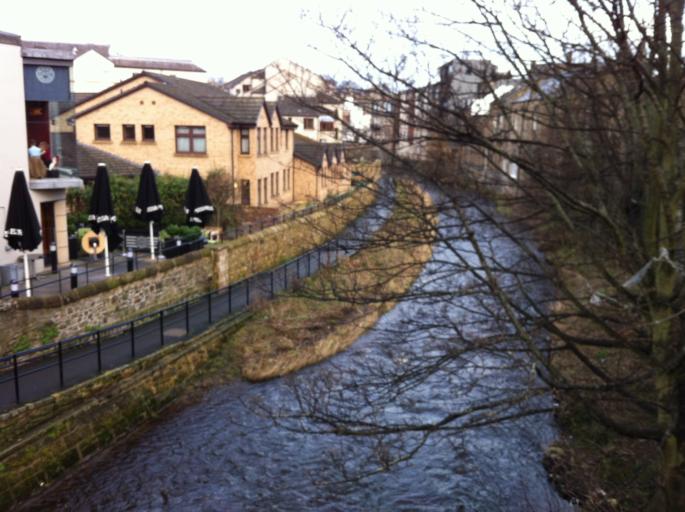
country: GB
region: Scotland
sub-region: Edinburgh
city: Edinburgh
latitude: 55.9580
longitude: -3.2086
